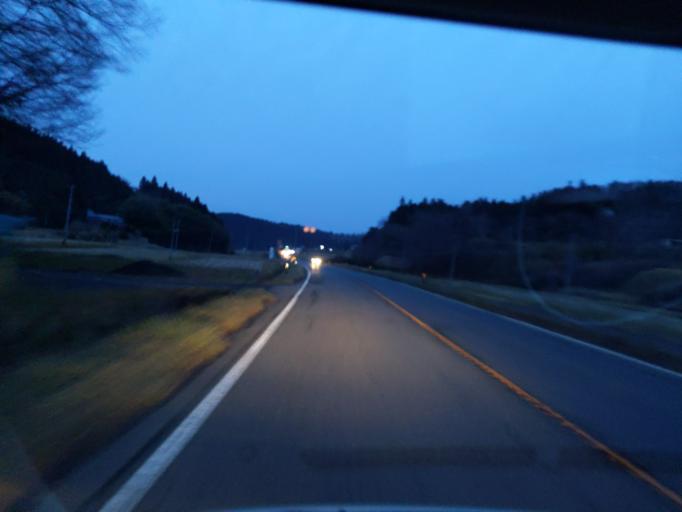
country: JP
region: Iwate
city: Ichinoseki
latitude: 38.8629
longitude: 141.1058
